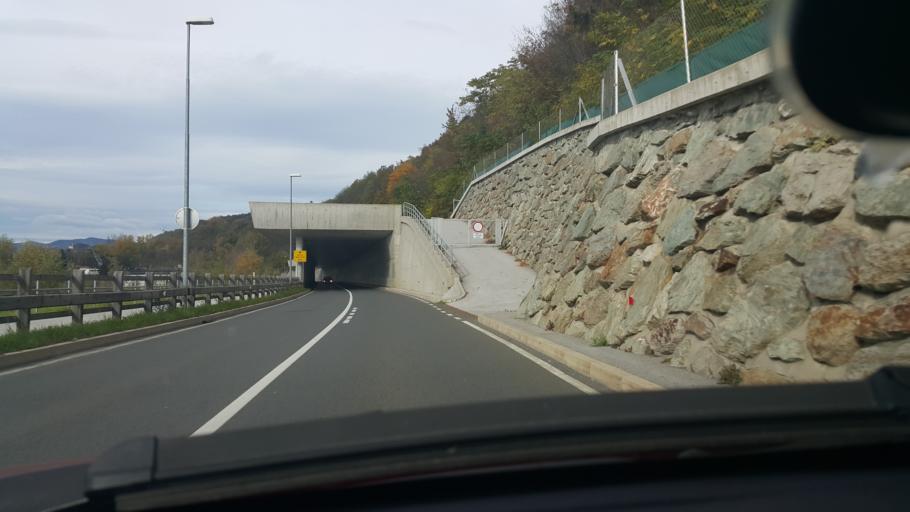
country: SI
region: Maribor
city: Maribor
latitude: 46.5594
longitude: 15.6785
